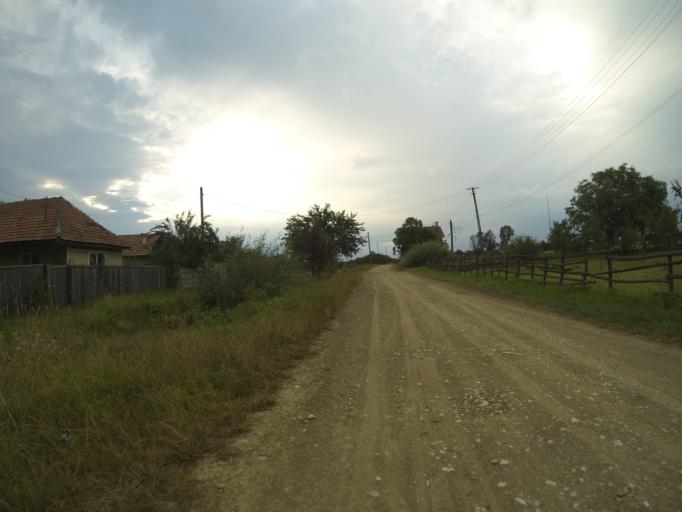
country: RO
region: Brasov
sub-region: Comuna Sinca Veche
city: Sinca Veche
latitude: 45.7688
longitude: 25.1734
